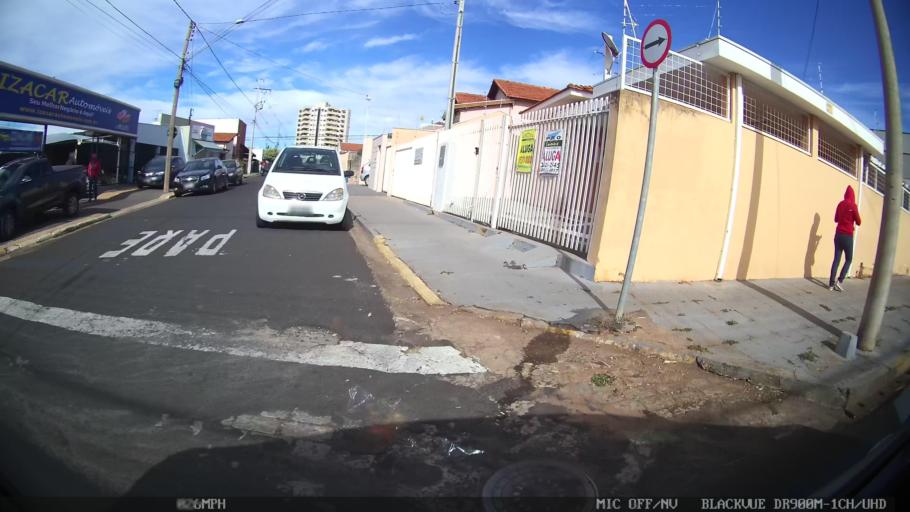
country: BR
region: Sao Paulo
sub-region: Catanduva
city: Catanduva
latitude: -21.1400
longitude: -48.9703
